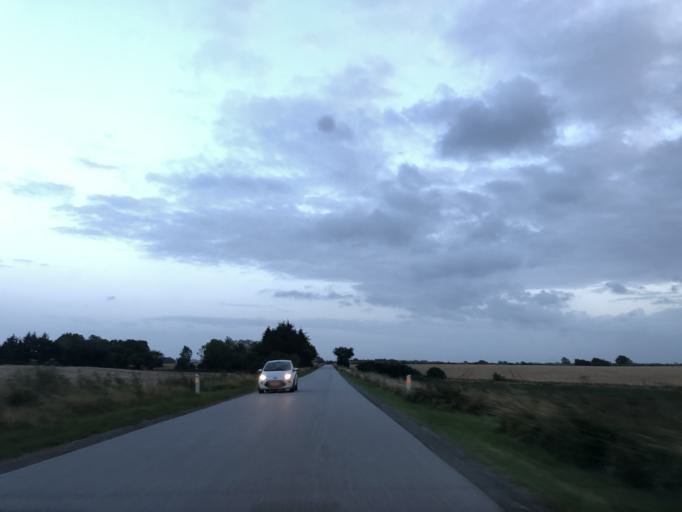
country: DK
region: South Denmark
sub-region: Haderslev Kommune
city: Starup
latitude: 55.2387
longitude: 9.6381
